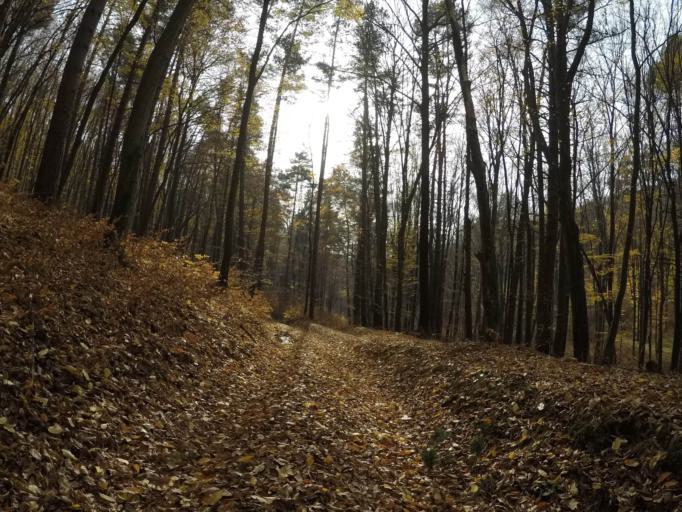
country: SK
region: Presovsky
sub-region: Okres Presov
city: Presov
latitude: 48.9524
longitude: 21.1836
